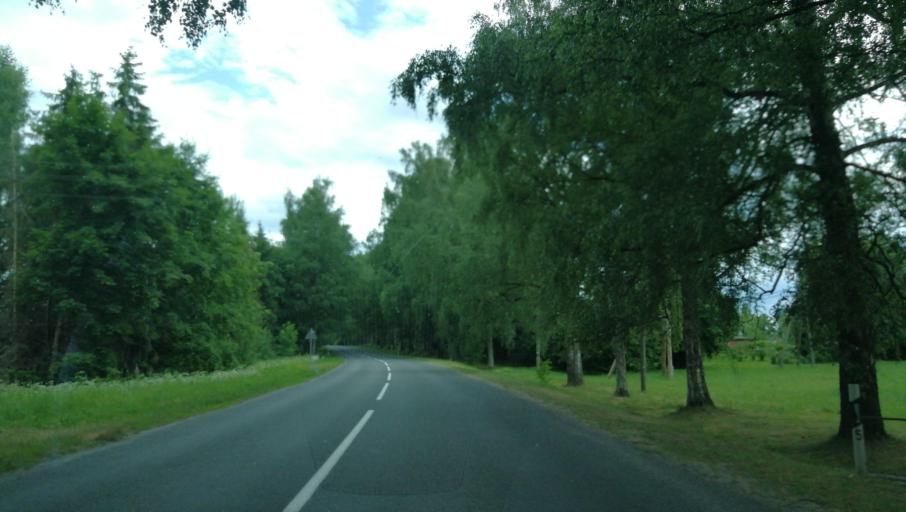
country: LV
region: Rujienas
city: Rujiena
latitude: 57.8598
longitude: 25.3739
